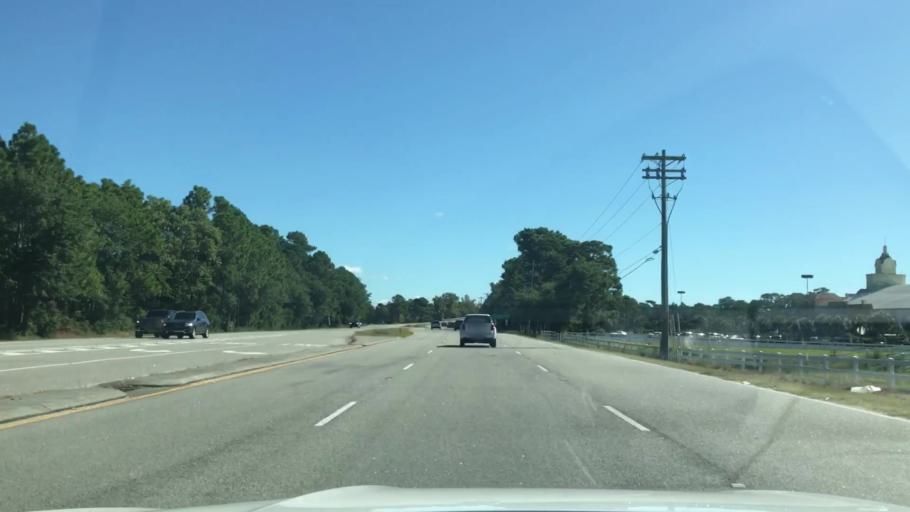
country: US
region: South Carolina
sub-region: Horry County
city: Myrtle Beach
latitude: 33.7646
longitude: -78.8115
